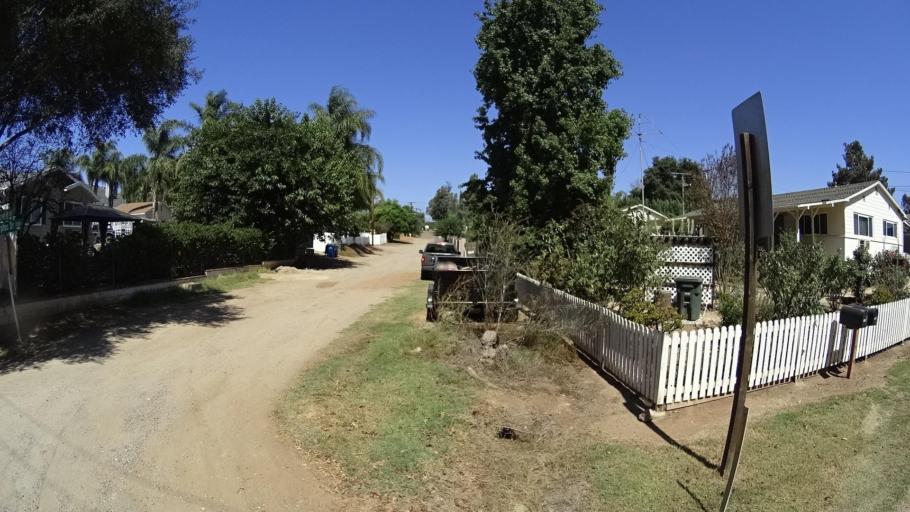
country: US
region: California
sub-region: San Diego County
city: Crest
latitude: 32.8059
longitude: -116.8652
